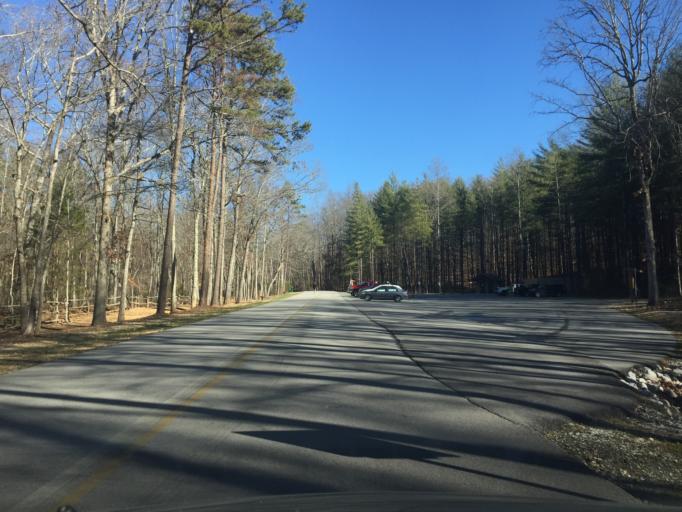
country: US
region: Tennessee
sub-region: Hamilton County
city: Harrison
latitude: 35.0844
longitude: -85.1167
